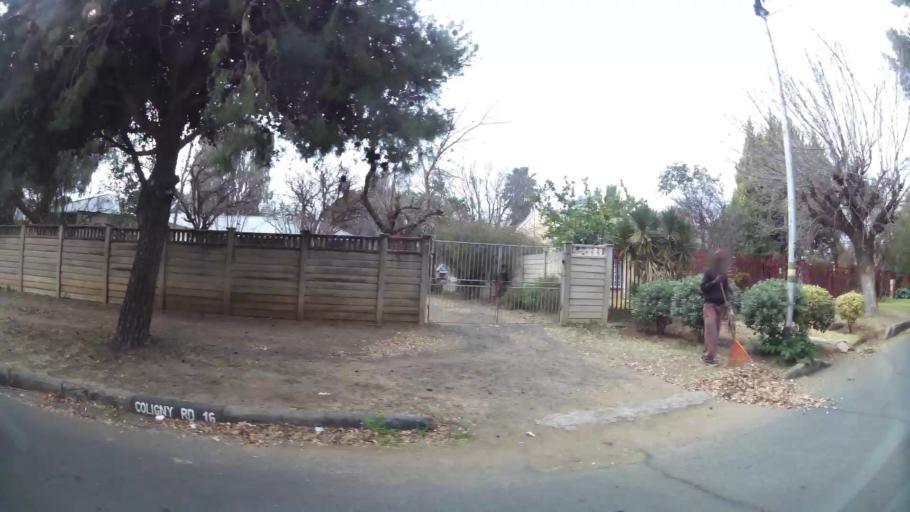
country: ZA
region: Orange Free State
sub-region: Mangaung Metropolitan Municipality
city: Bloemfontein
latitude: -29.1218
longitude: 26.1968
